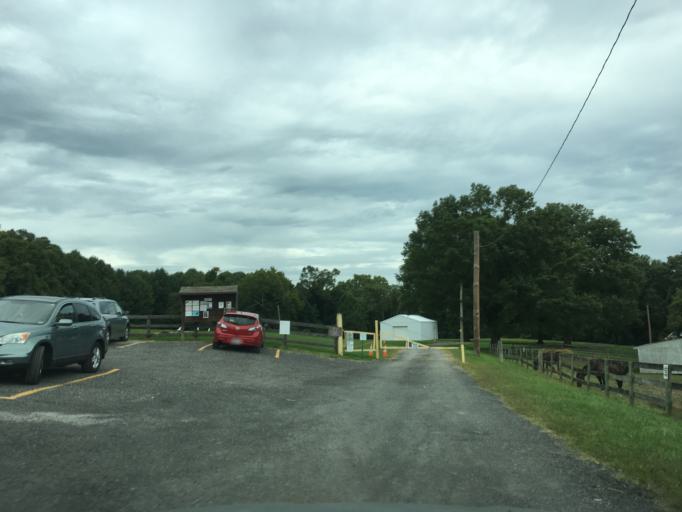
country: US
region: Maryland
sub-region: Baltimore County
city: Carney
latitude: 39.4142
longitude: -76.5084
